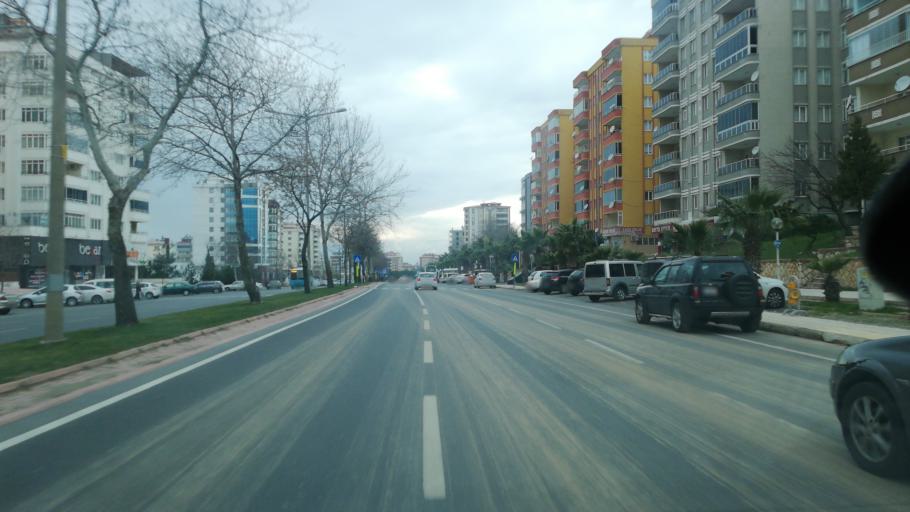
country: TR
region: Kahramanmaras
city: Kahramanmaras
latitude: 37.5927
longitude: 36.8633
